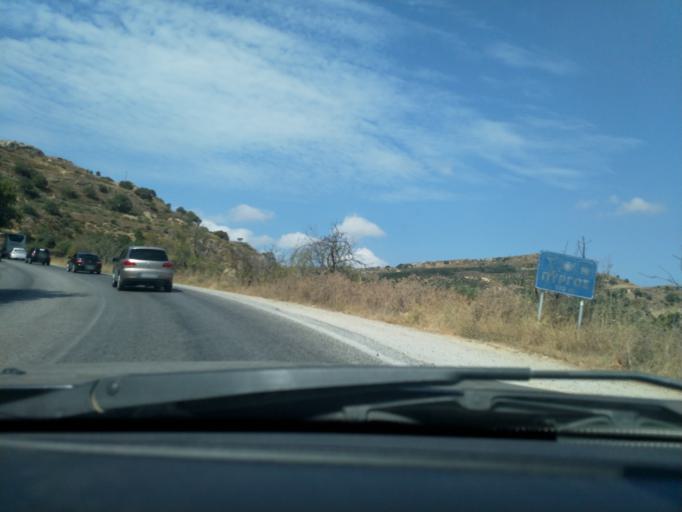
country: GR
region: Crete
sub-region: Nomos Rethymnis
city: Atsipopoulon
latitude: 35.2586
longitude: 24.4774
